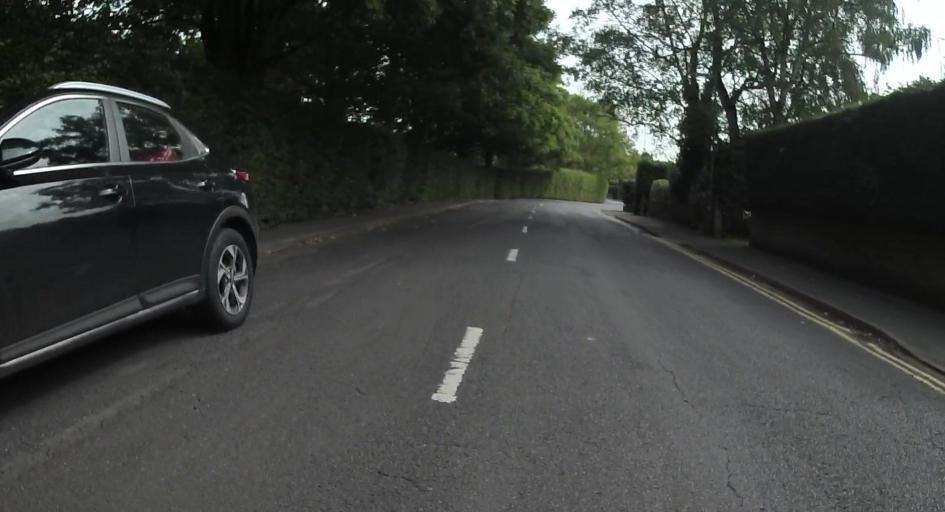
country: GB
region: England
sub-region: Surrey
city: Woking
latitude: 51.3290
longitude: -0.5731
